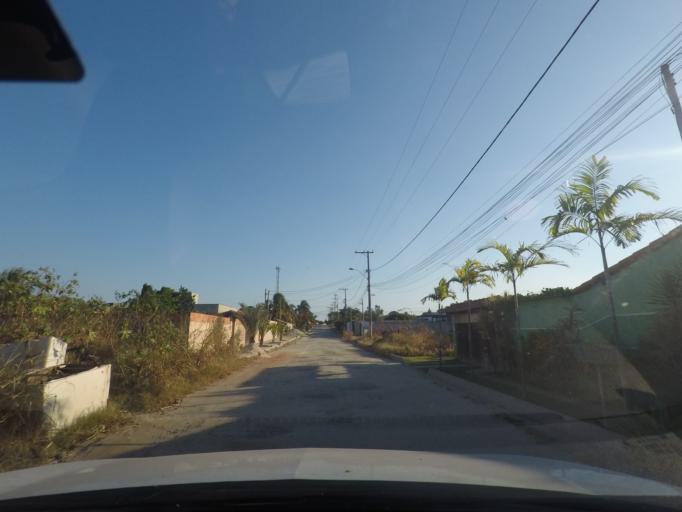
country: BR
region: Rio de Janeiro
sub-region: Marica
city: Marica
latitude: -22.9656
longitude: -42.9343
